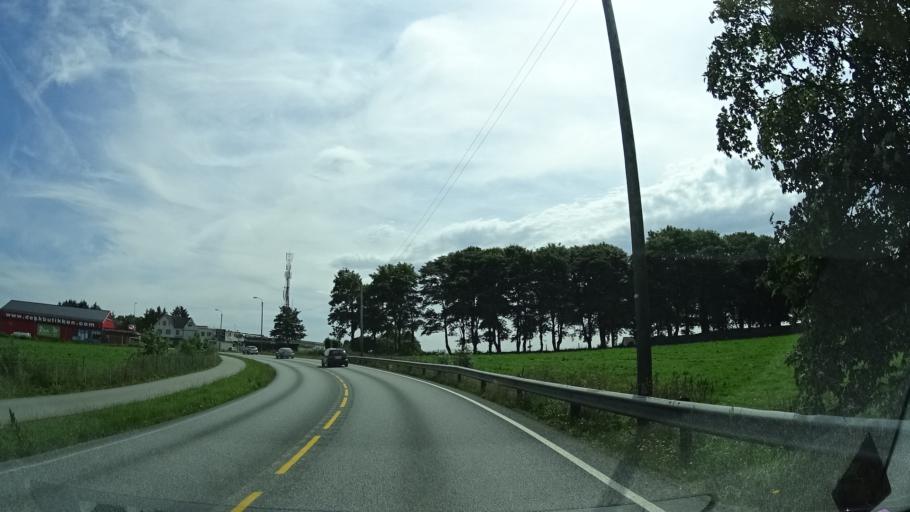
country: NO
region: Rogaland
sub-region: Randaberg
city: Randaberg
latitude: 58.9839
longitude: 5.6665
